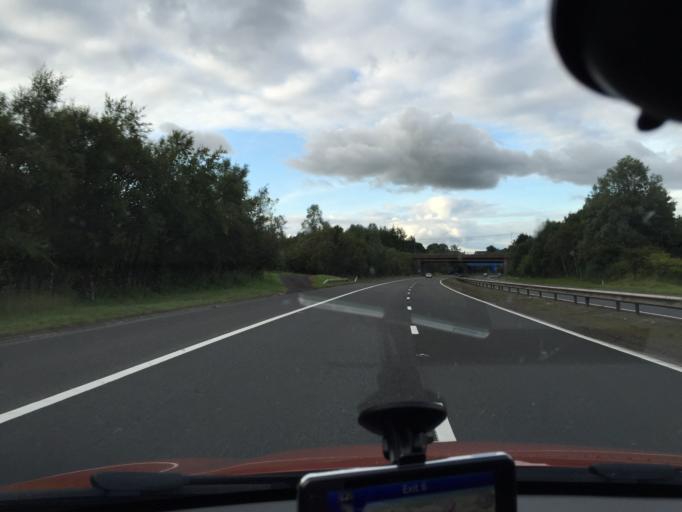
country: GB
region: Scotland
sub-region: North Lanarkshire
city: Chryston
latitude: 55.8822
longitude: -4.0818
